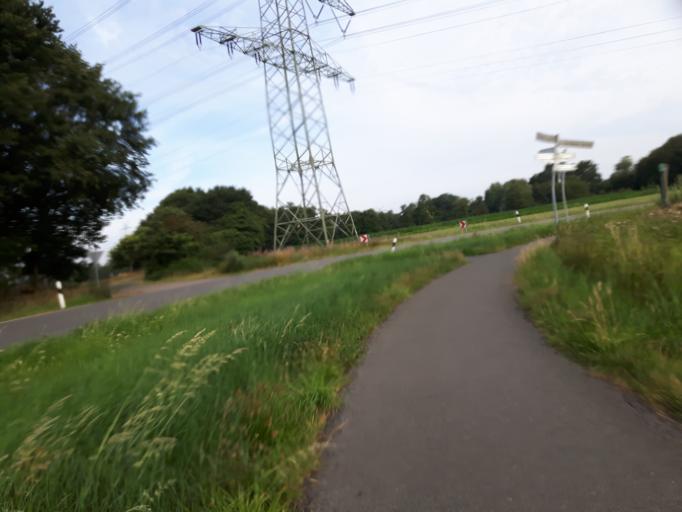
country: DE
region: Lower Saxony
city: Delmenhorst
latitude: 53.0882
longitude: 8.6063
